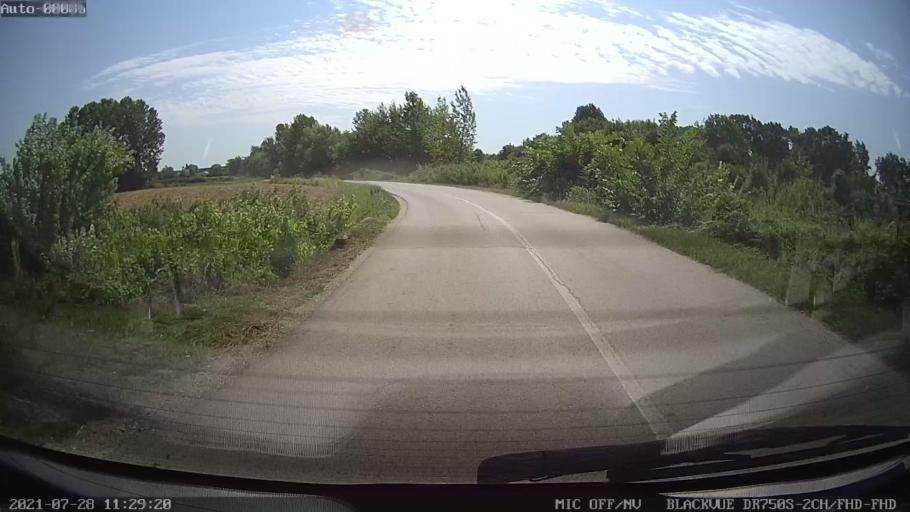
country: HR
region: Varazdinska
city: Jalzabet
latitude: 46.2779
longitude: 16.4230
